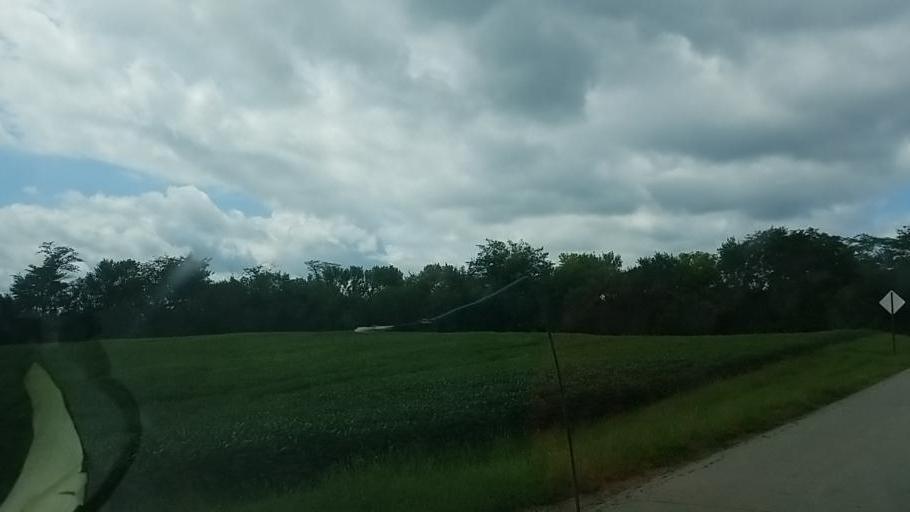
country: US
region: Ohio
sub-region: Madison County
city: Bethel
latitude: 39.6893
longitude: -83.4667
